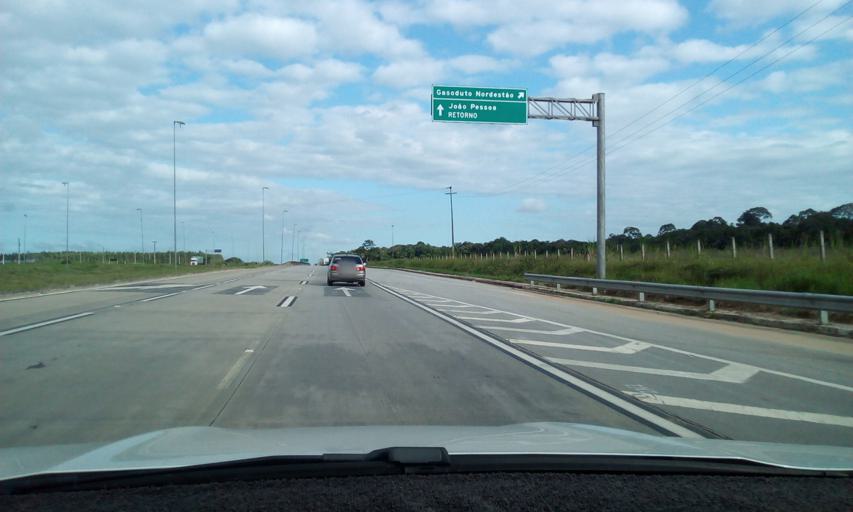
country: BR
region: Paraiba
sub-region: Cruz Do Espirito Santo
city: Cruz do Espirito Santo
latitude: -6.9900
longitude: -35.0716
